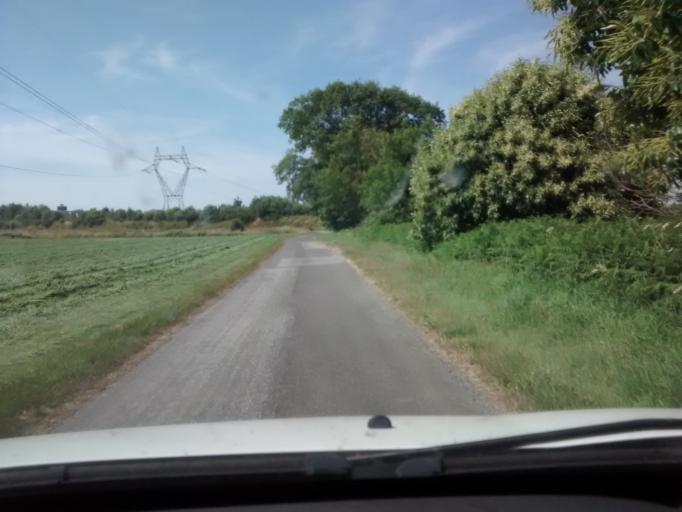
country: FR
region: Brittany
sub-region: Departement d'Ille-et-Vilaine
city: Acigne
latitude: 48.1129
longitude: -1.5589
